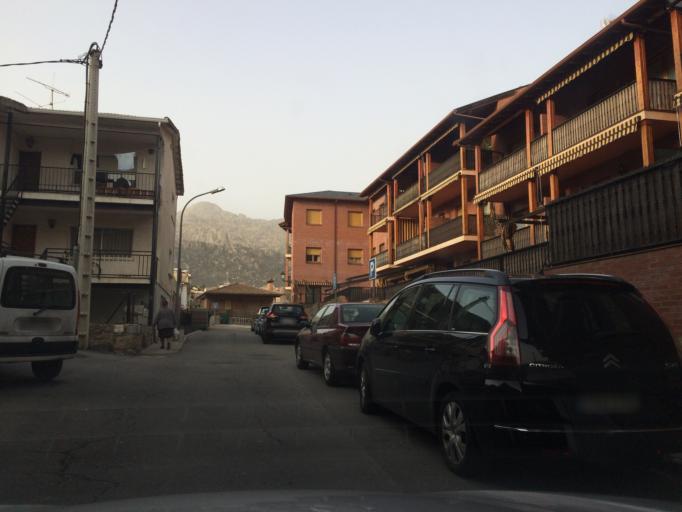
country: ES
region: Madrid
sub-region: Provincia de Madrid
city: Manzanares el Real
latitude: 40.7264
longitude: -3.8667
